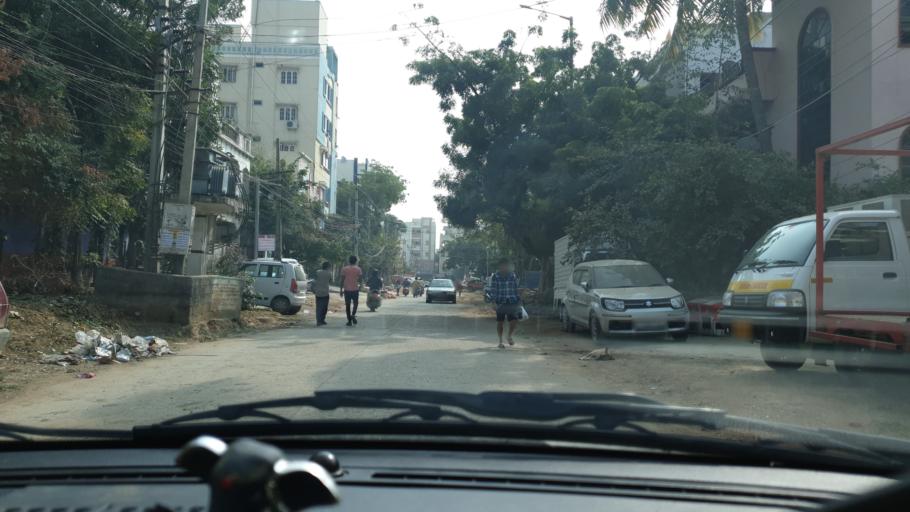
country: IN
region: Telangana
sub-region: Rangareddi
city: Kukatpalli
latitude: 17.4844
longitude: 78.4070
